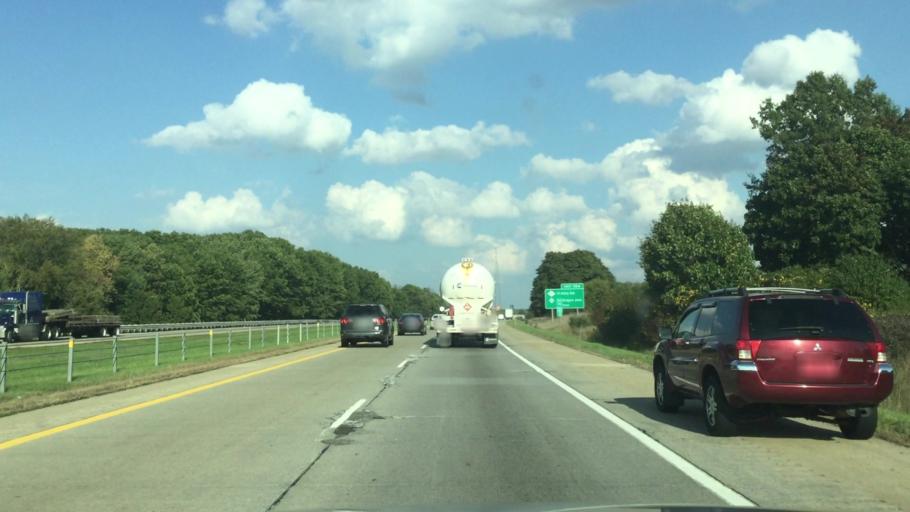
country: US
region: Michigan
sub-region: Calhoun County
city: Brownlee Park
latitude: 42.2944
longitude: -85.1018
